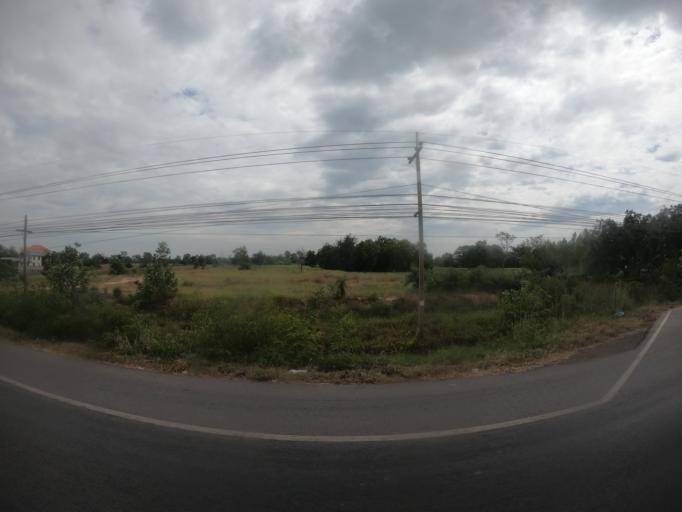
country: TH
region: Maha Sarakham
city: Kantharawichai
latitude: 16.2919
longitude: 103.2950
